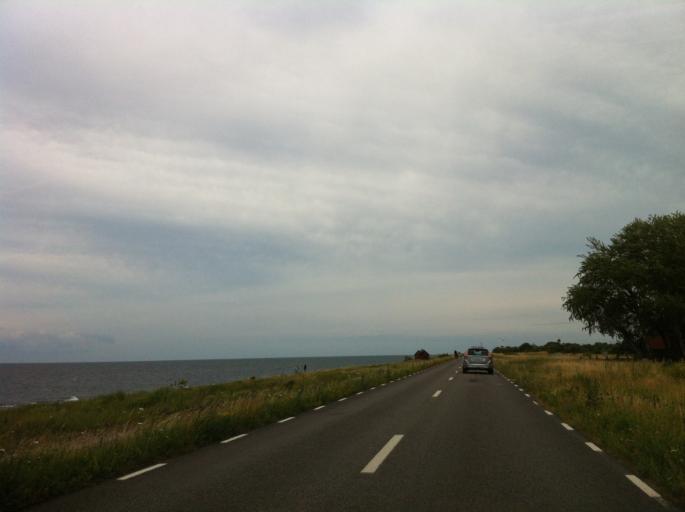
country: SE
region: Kalmar
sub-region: Vasterviks Kommun
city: Vaestervik
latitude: 57.3345
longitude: 17.0108
